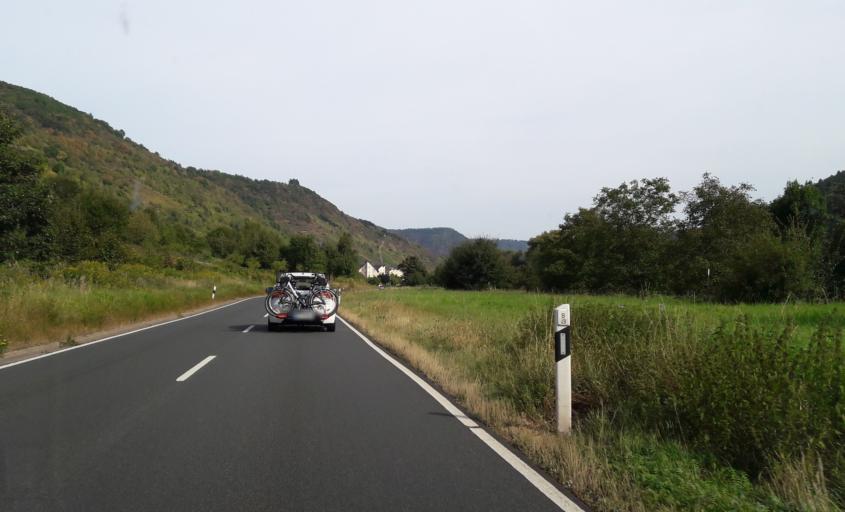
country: DE
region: Rheinland-Pfalz
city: Bullay
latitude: 50.0693
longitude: 7.1293
